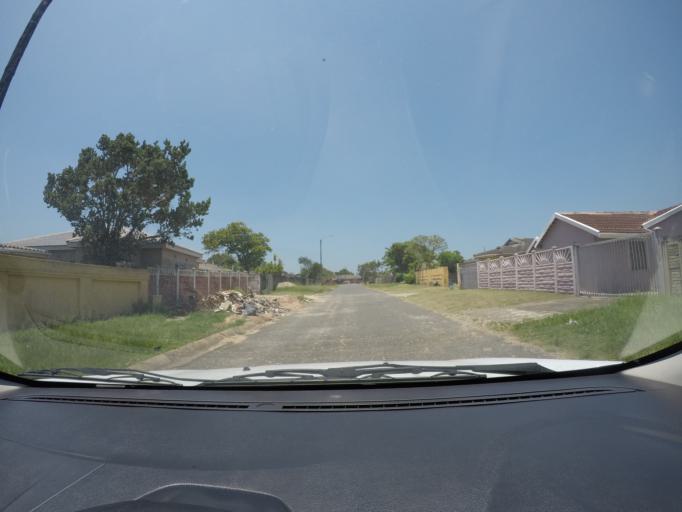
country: ZA
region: KwaZulu-Natal
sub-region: uThungulu District Municipality
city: eSikhawini
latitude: -28.8767
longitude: 31.9053
